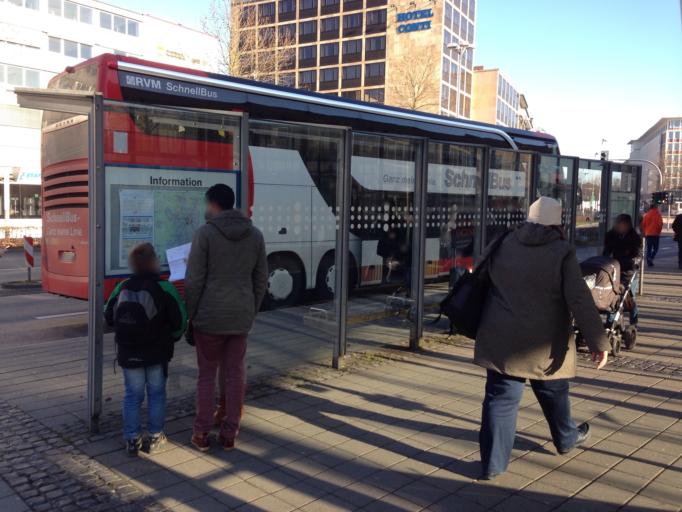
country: DE
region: North Rhine-Westphalia
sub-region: Regierungsbezirk Munster
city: Muenster
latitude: 51.9563
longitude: 7.6339
